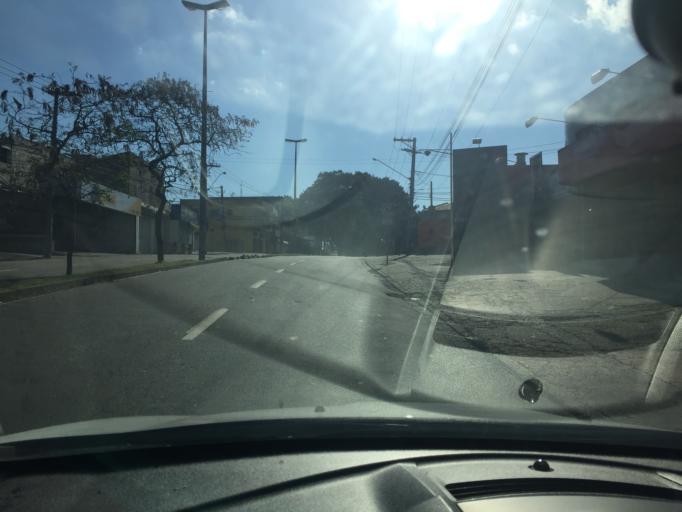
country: BR
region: Sao Paulo
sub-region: Varzea Paulista
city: Varzea Paulista
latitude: -23.2080
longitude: -46.8568
